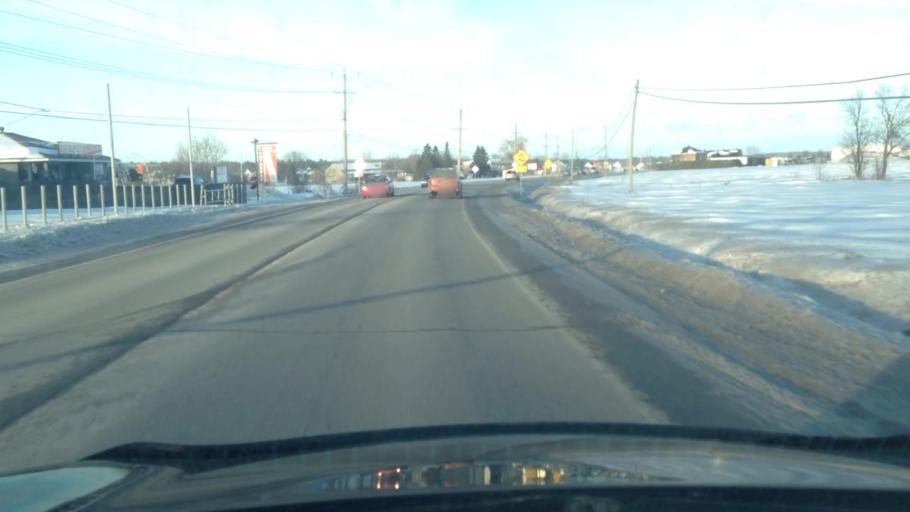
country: CA
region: Quebec
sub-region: Lanaudiere
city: Saint-Lin-Laurentides
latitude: 45.8890
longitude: -73.7579
